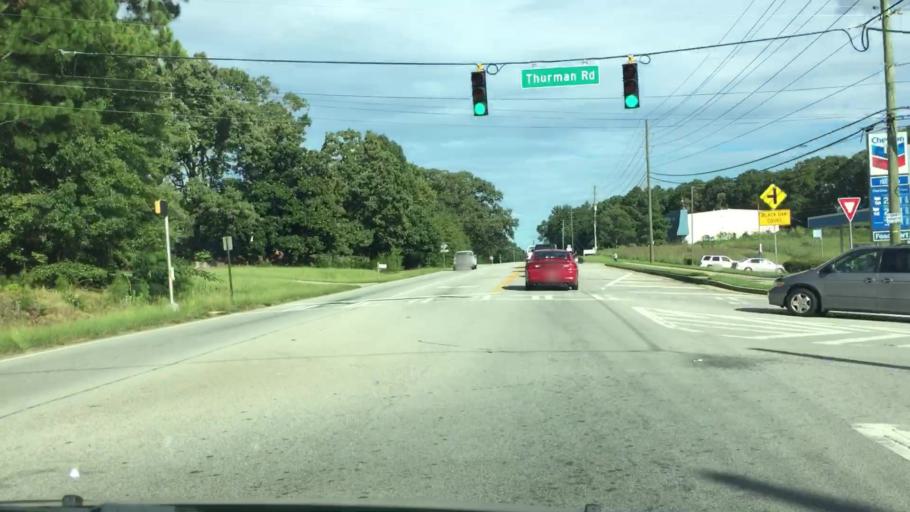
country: US
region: Georgia
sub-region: Henry County
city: Stockbridge
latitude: 33.6082
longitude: -84.2245
